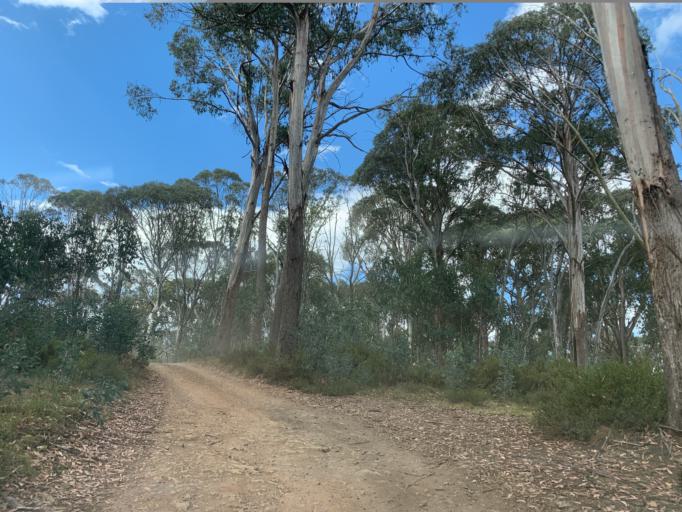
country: AU
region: Victoria
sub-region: Mansfield
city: Mansfield
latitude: -37.1038
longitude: 146.5383
